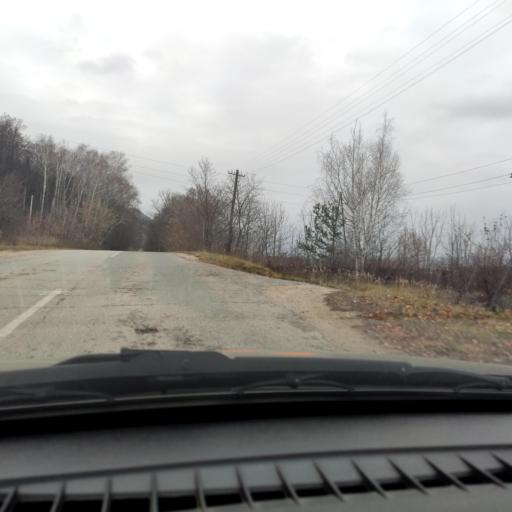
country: RU
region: Samara
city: Pribrezhnyy
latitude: 53.4385
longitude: 49.7290
